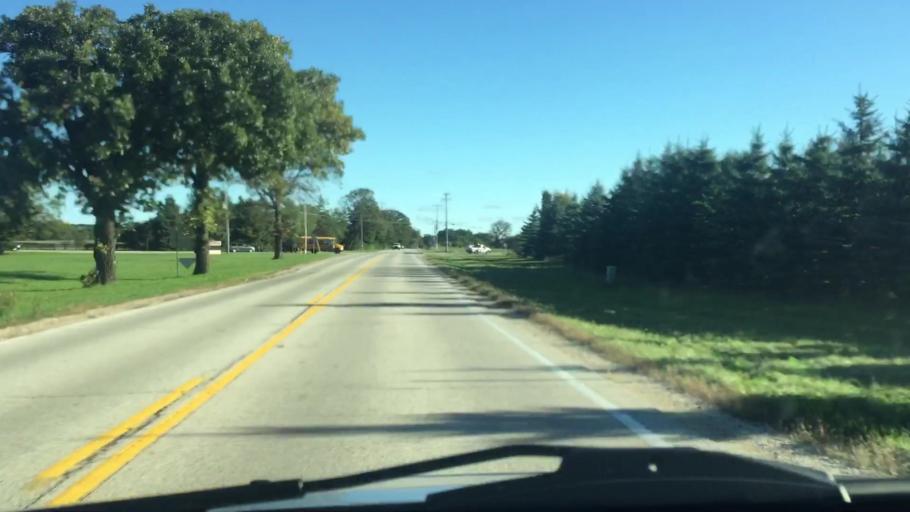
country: US
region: Wisconsin
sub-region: Waukesha County
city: North Prairie
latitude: 42.9726
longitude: -88.3995
